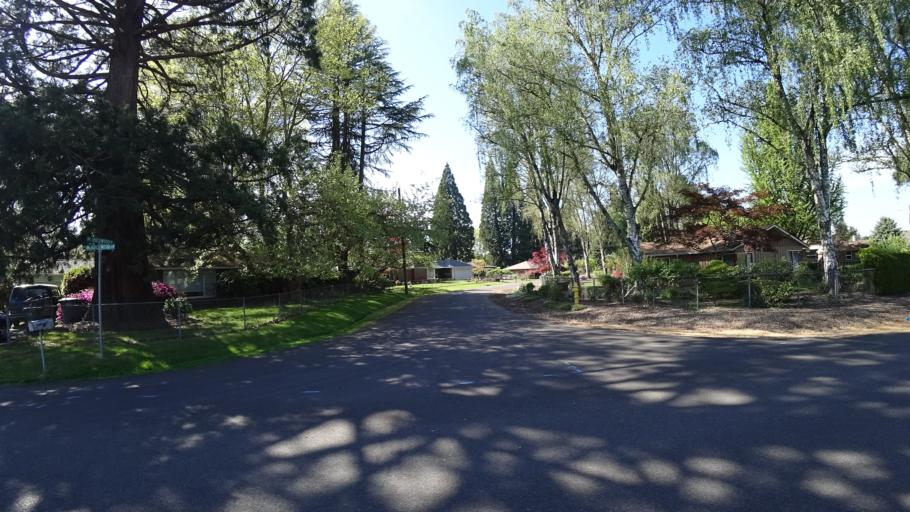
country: US
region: Oregon
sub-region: Washington County
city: Hillsboro
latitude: 45.5272
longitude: -122.9769
